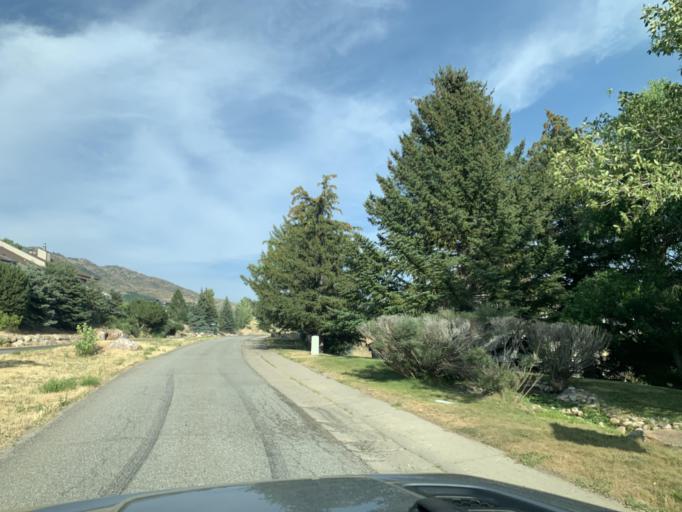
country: US
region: Utah
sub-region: Weber County
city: Wolf Creek
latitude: 41.3299
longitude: -111.8233
